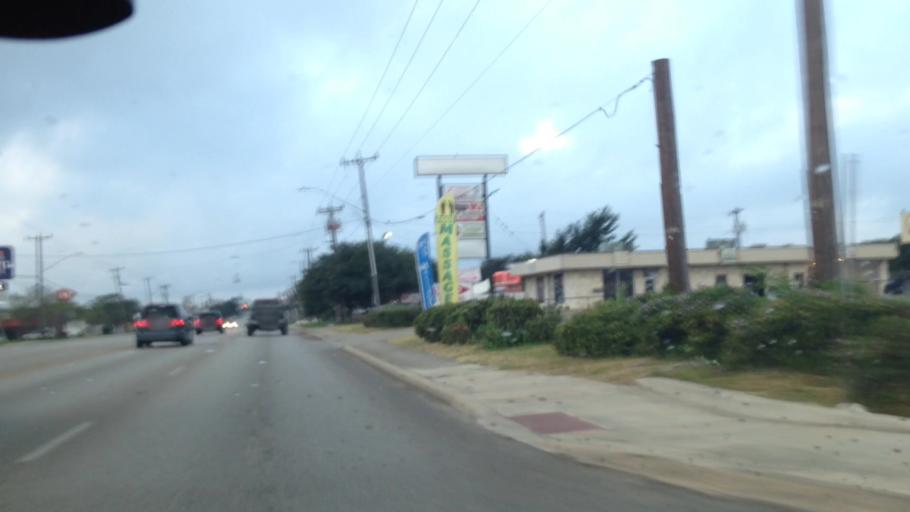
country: US
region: Texas
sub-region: Bexar County
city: Windcrest
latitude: 29.5620
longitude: -98.3929
